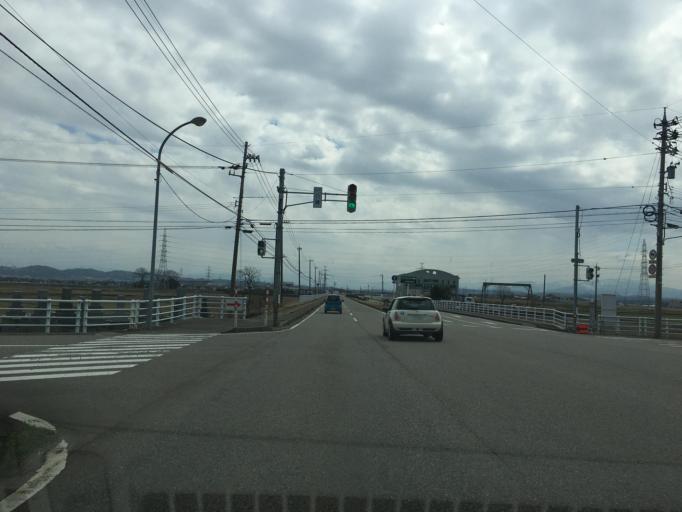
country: JP
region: Toyama
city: Kuragaki-kosugi
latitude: 36.7427
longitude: 137.1298
